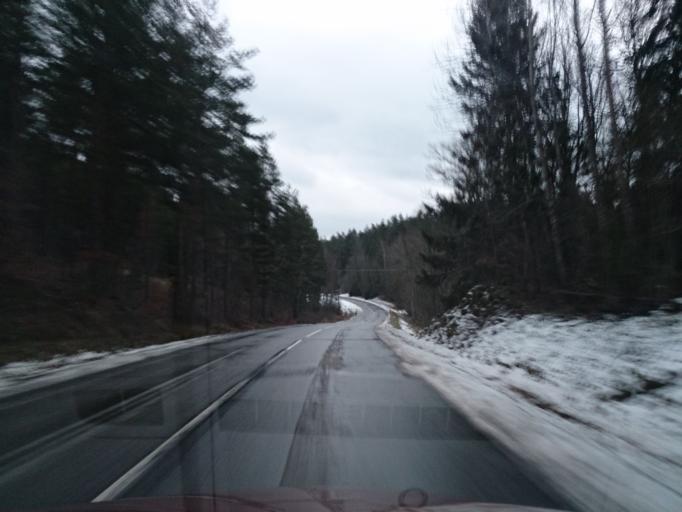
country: SE
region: OEstergoetland
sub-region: Norrkopings Kommun
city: Kimstad
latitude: 58.3858
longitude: 15.9986
